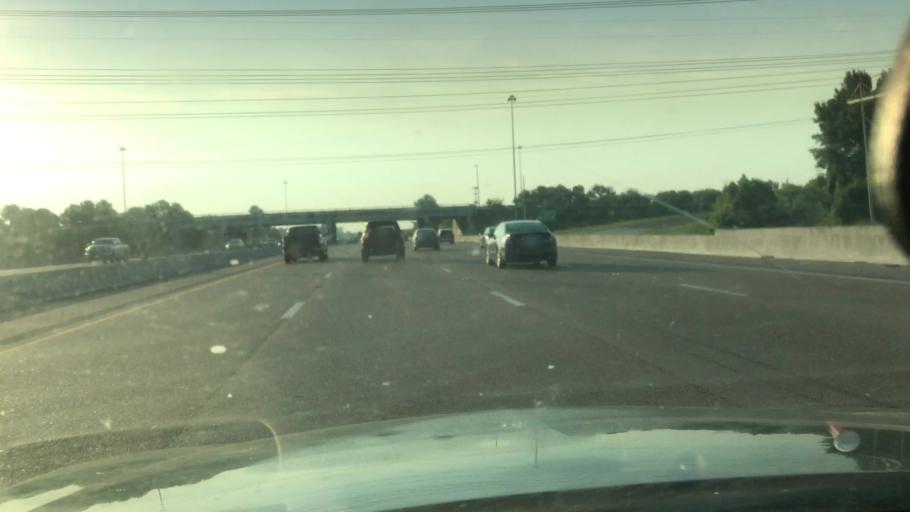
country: US
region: Mississippi
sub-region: De Soto County
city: Southaven
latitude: 35.0802
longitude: -89.9337
